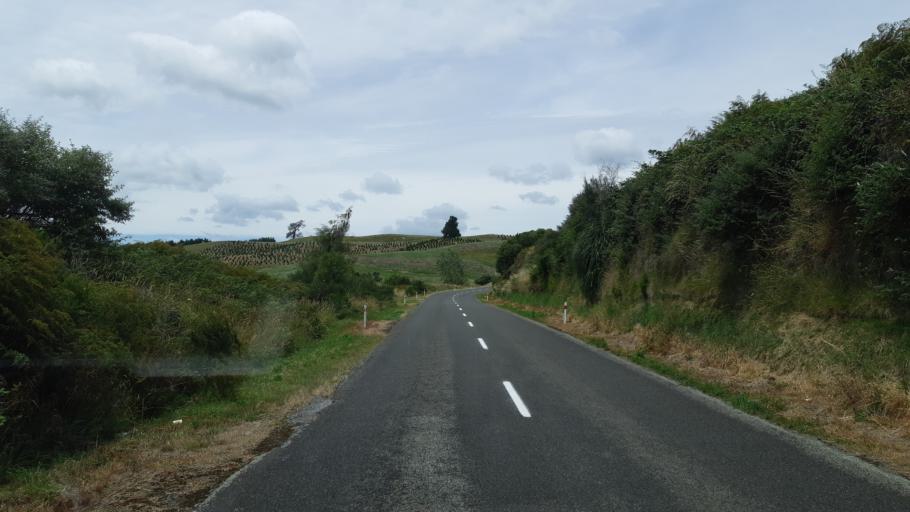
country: NZ
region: Waikato
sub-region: Taupo District
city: Taupo
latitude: -38.6267
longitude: 176.1504
